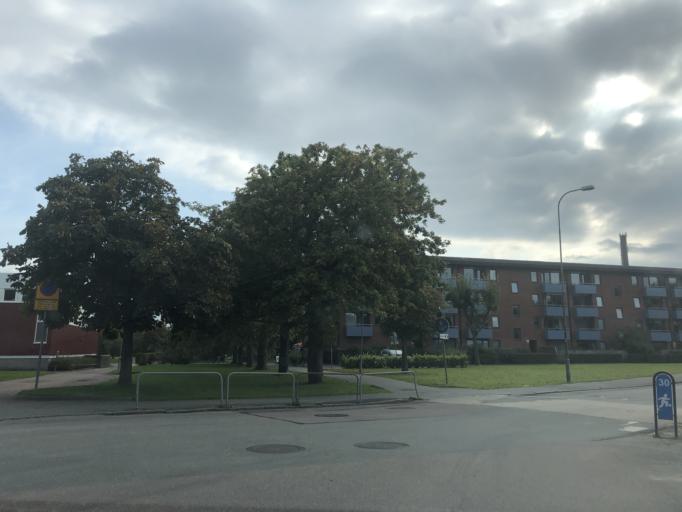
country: SE
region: Vaestra Goetaland
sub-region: Goteborg
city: Majorna
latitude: 57.6518
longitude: 11.8905
